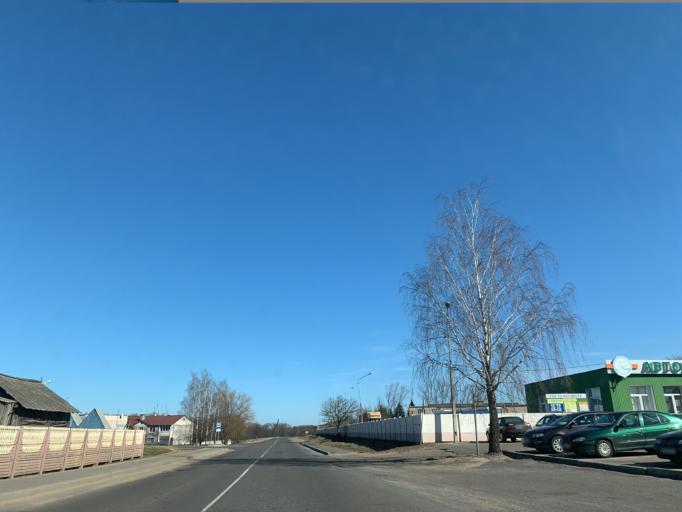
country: BY
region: Minsk
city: Nyasvizh
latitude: 53.2153
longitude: 26.6995
